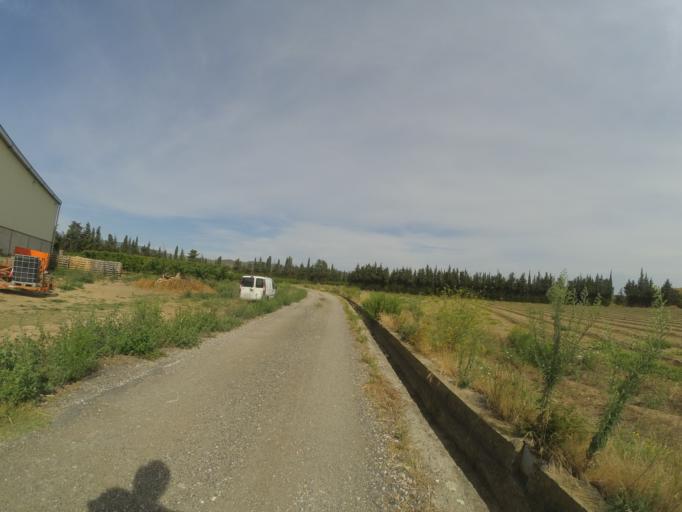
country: FR
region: Languedoc-Roussillon
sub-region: Departement des Pyrenees-Orientales
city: Ille-sur-Tet
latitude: 42.6573
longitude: 2.6330
